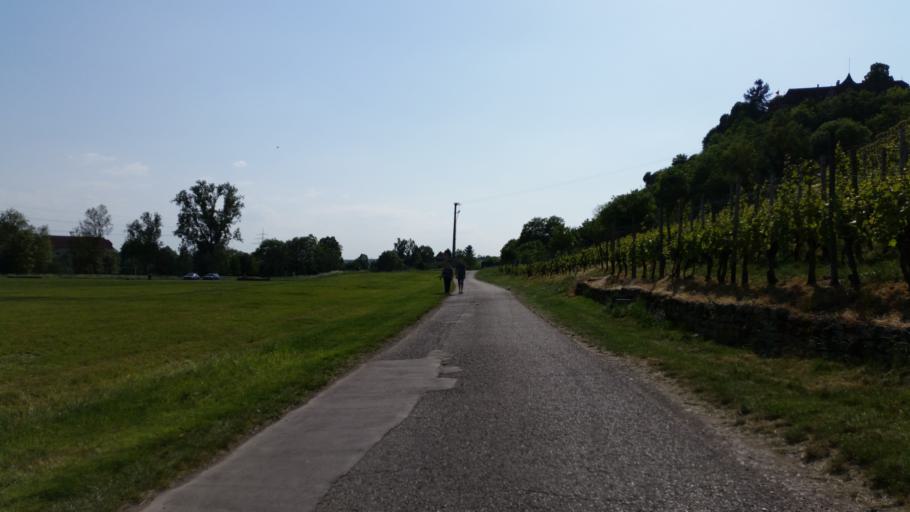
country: DE
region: Baden-Wuerttemberg
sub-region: Regierungsbezirk Stuttgart
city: Pleidelsheim
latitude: 48.9743
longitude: 9.2046
